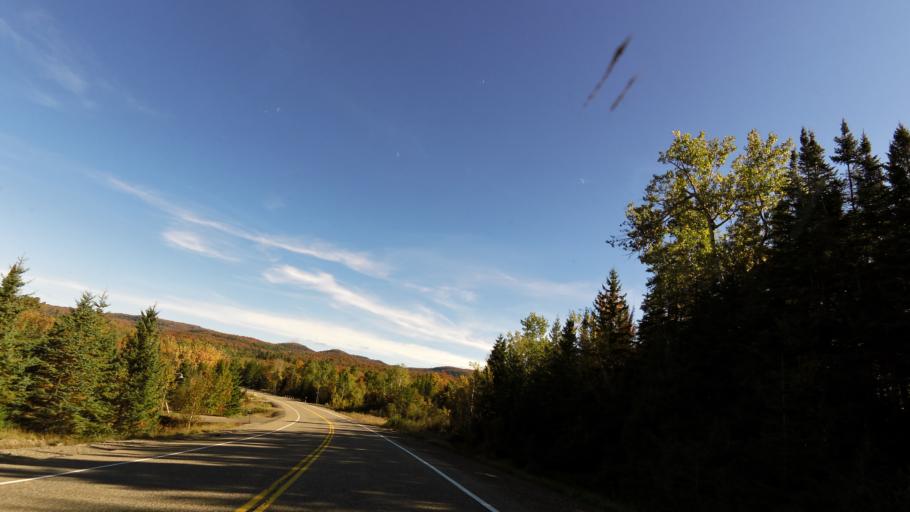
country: CA
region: Ontario
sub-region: Algoma
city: Sault Ste. Marie
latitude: 46.8673
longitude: -84.3554
